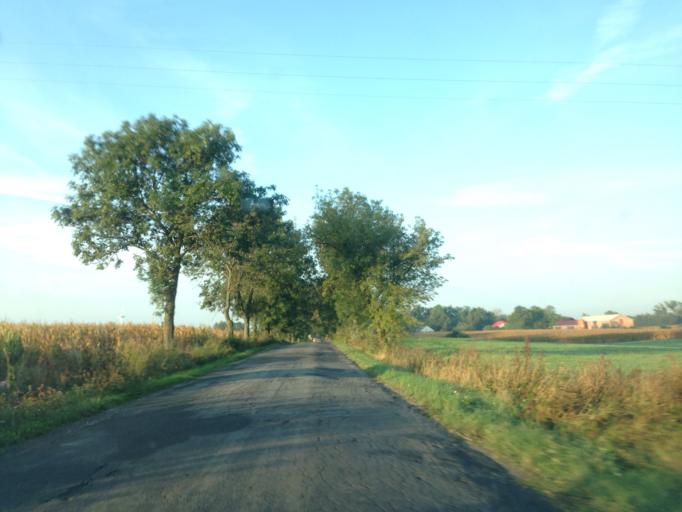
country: PL
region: Kujawsko-Pomorskie
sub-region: Powiat golubsko-dobrzynski
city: Radomin
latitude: 53.1145
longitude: 19.1528
